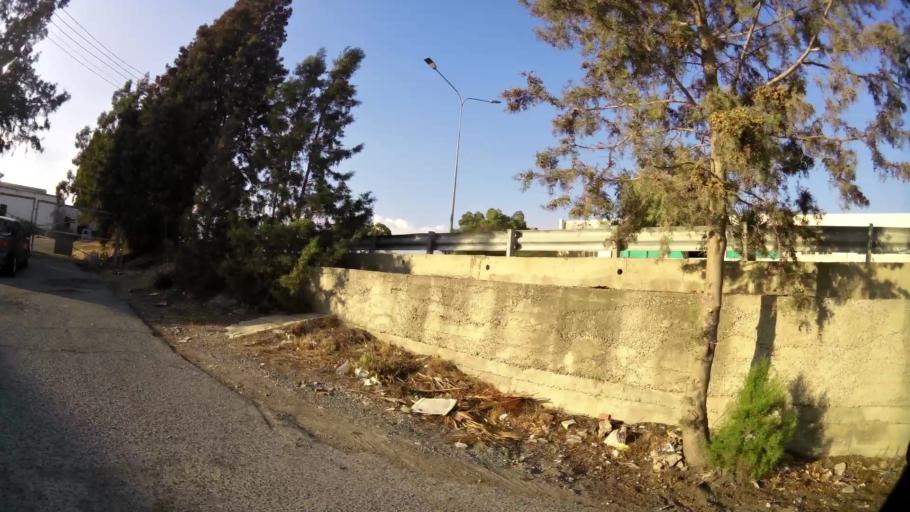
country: CY
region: Larnaka
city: Larnaca
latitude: 34.9266
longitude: 33.6064
